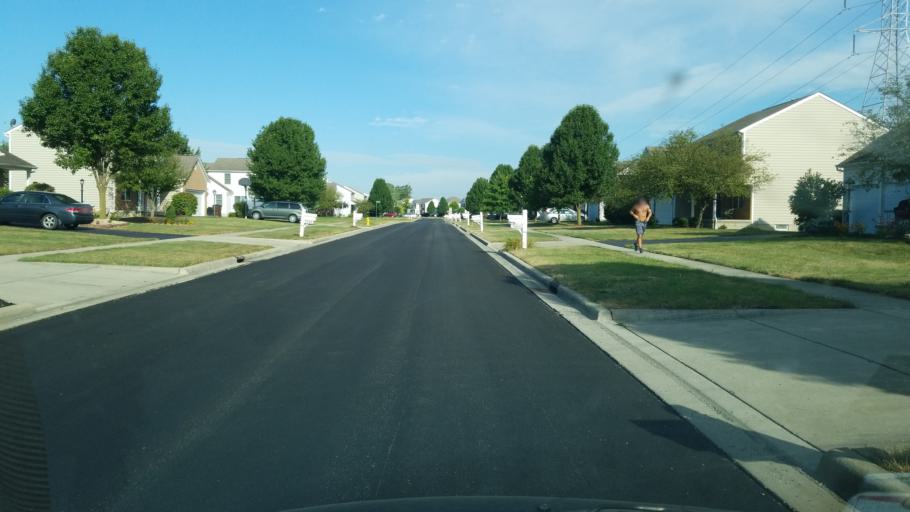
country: US
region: Ohio
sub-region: Delaware County
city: Lewis Center
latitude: 40.1764
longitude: -83.0029
